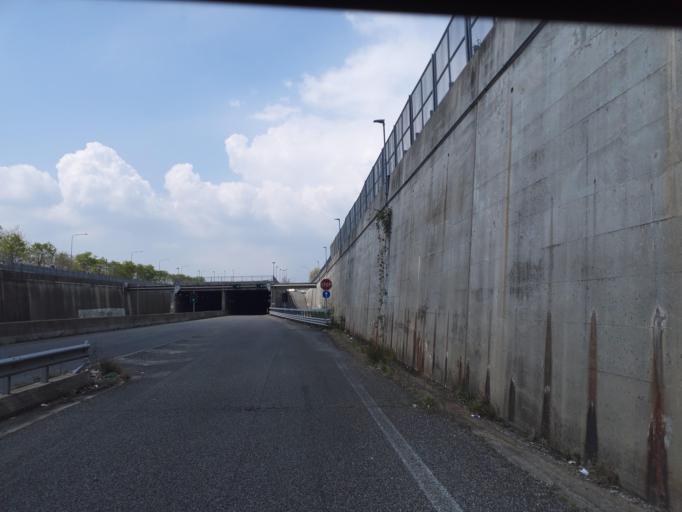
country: IT
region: Piedmont
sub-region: Provincia di Biella
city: Ponderano
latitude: 45.5487
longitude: 8.0629
